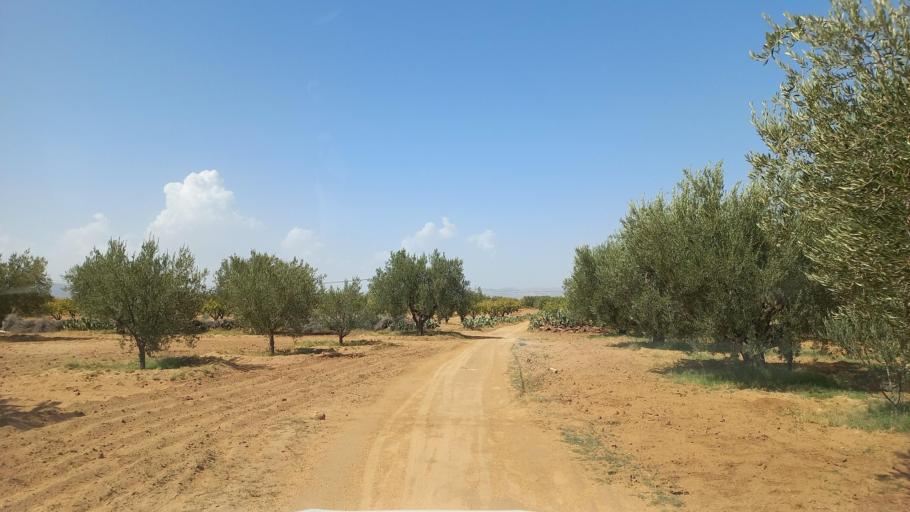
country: TN
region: Al Qasrayn
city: Kasserine
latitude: 35.2228
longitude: 9.0429
